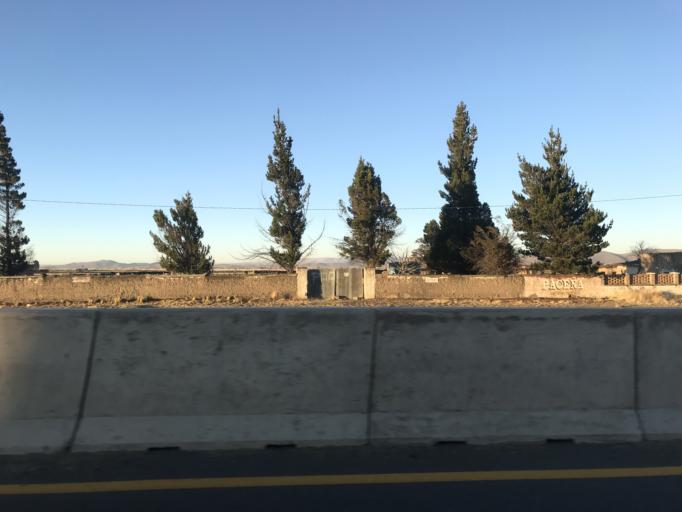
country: BO
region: La Paz
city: Batallas
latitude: -16.3002
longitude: -68.4919
